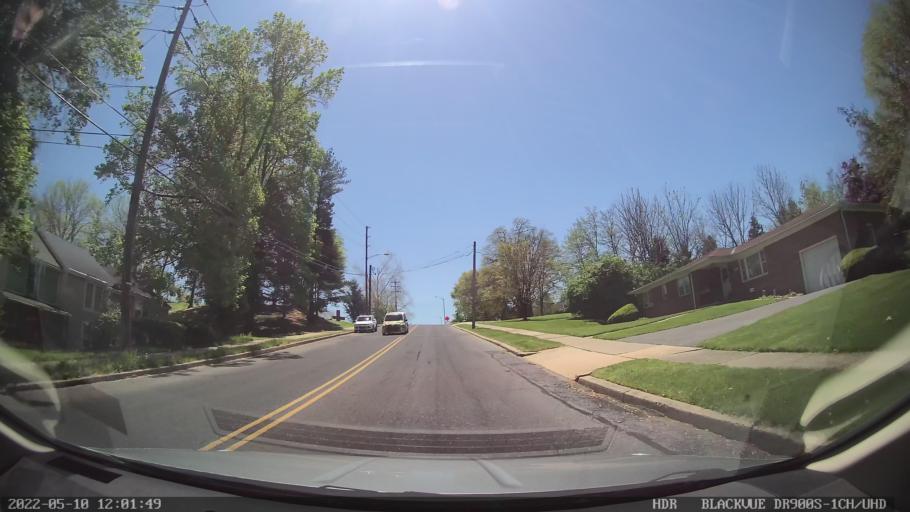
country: US
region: Pennsylvania
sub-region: Berks County
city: West Reading
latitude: 40.3246
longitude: -75.9483
